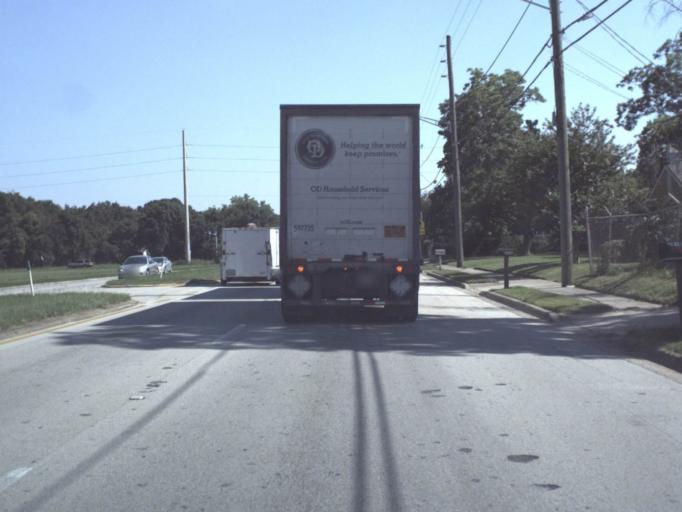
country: US
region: Florida
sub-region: Duval County
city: Jacksonville
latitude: 30.3529
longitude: -81.7312
